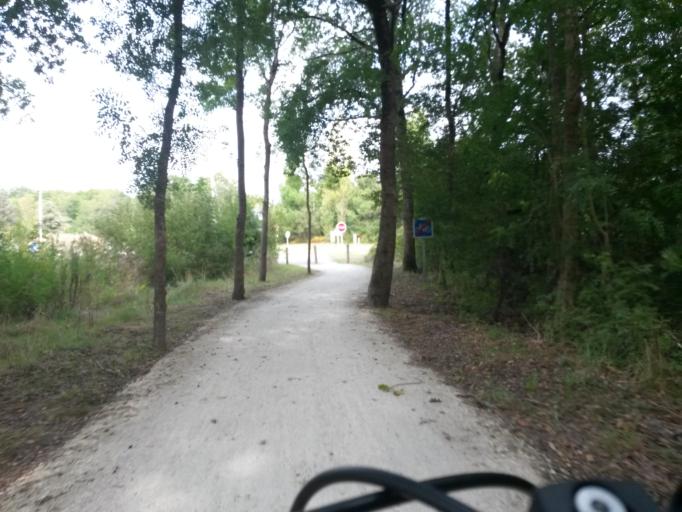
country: FR
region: Poitou-Charentes
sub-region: Departement de la Charente-Maritime
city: Dolus-d'Oleron
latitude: 45.8887
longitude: -1.2345
